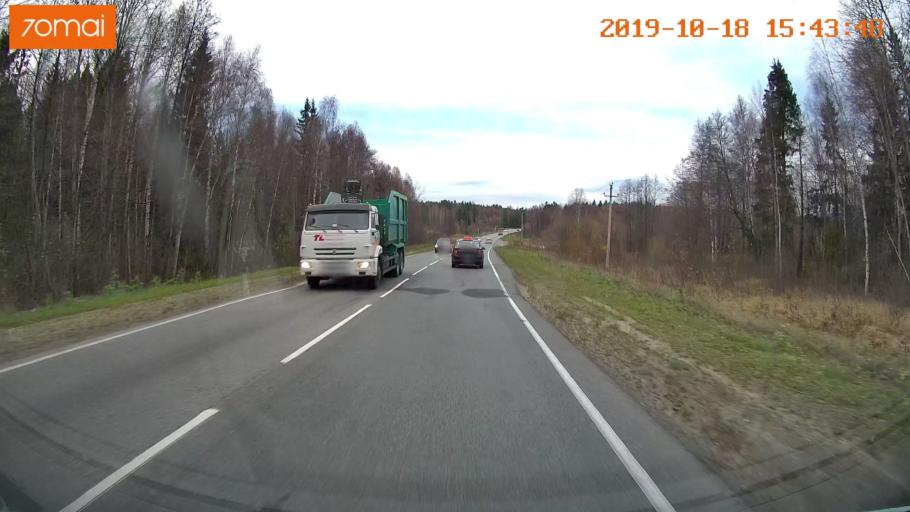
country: RU
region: Vladimir
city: Golovino
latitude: 55.9731
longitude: 40.5476
